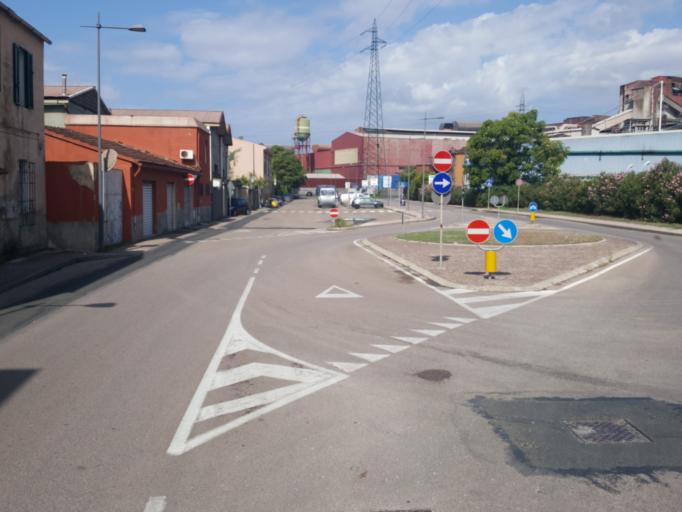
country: IT
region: Tuscany
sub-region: Provincia di Livorno
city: Piombino
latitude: 42.9263
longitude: 10.5346
